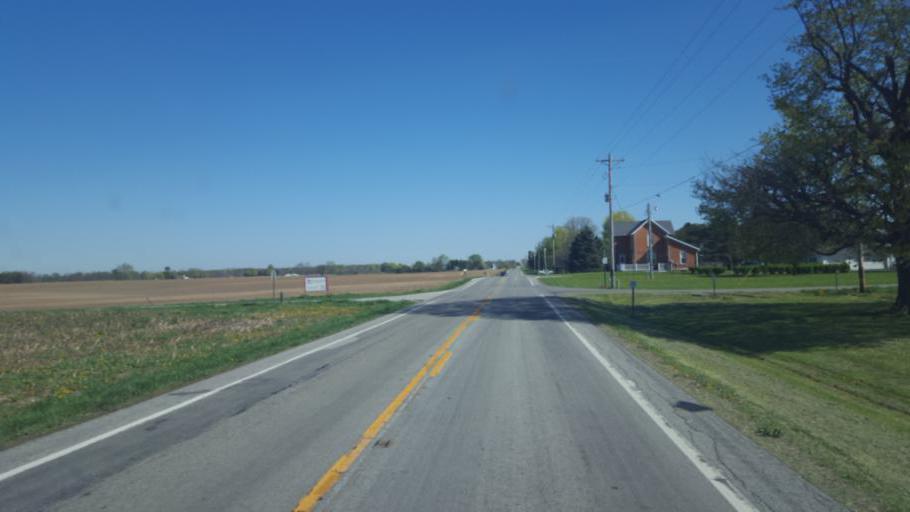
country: US
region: Ohio
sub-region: Seneca County
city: Tiffin
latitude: 40.9781
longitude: -83.1703
